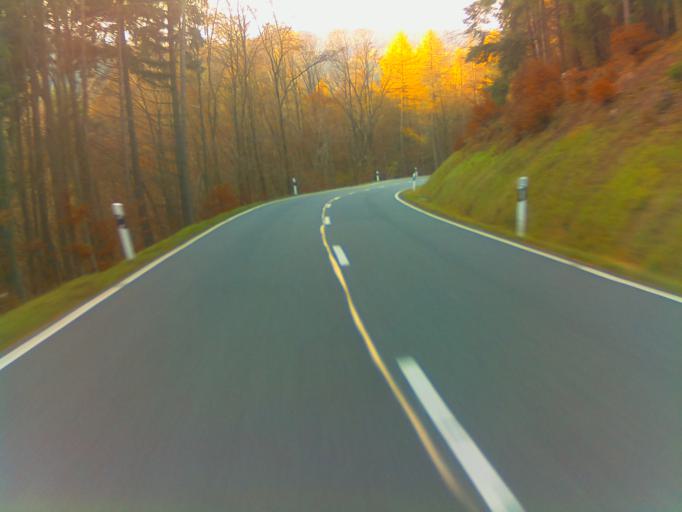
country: DE
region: Hesse
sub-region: Regierungsbezirk Darmstadt
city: Hesseneck
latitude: 49.5539
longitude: 9.1227
